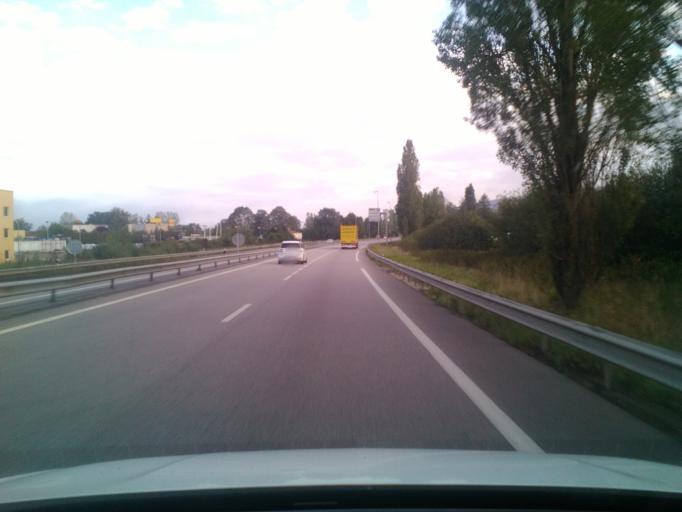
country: FR
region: Lorraine
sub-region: Departement des Vosges
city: Saint-Die-des-Vosges
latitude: 48.2881
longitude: 6.9317
